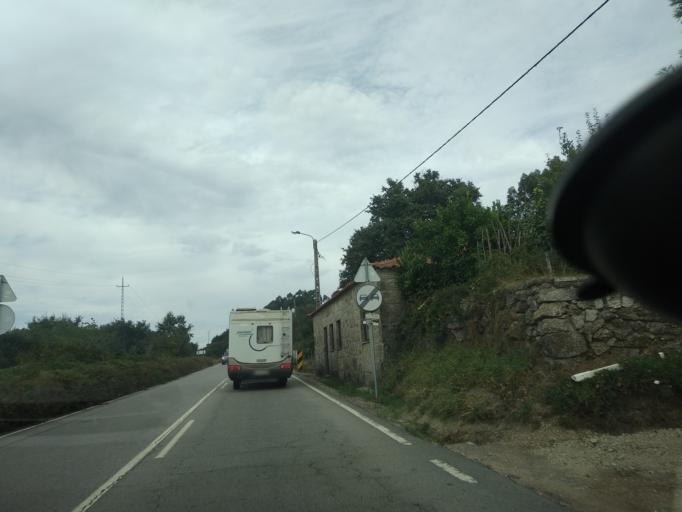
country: PT
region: Braga
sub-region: Vieira do Minho
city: Real
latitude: 41.6243
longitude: -8.2065
